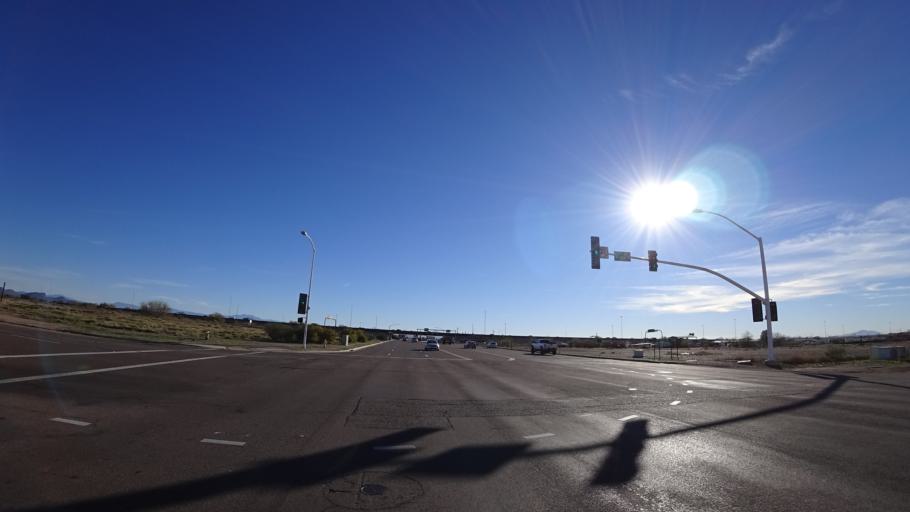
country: US
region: Arizona
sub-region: Maricopa County
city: Scottsdale
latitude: 33.4659
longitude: -111.8919
